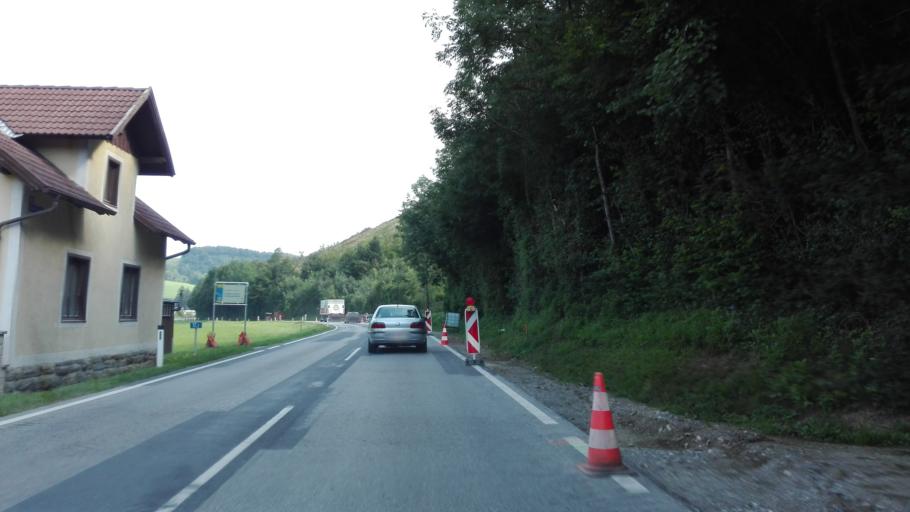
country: AT
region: Lower Austria
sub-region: Politischer Bezirk Sankt Polten
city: Rabenstein an der Pielach
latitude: 48.0728
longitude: 15.4807
